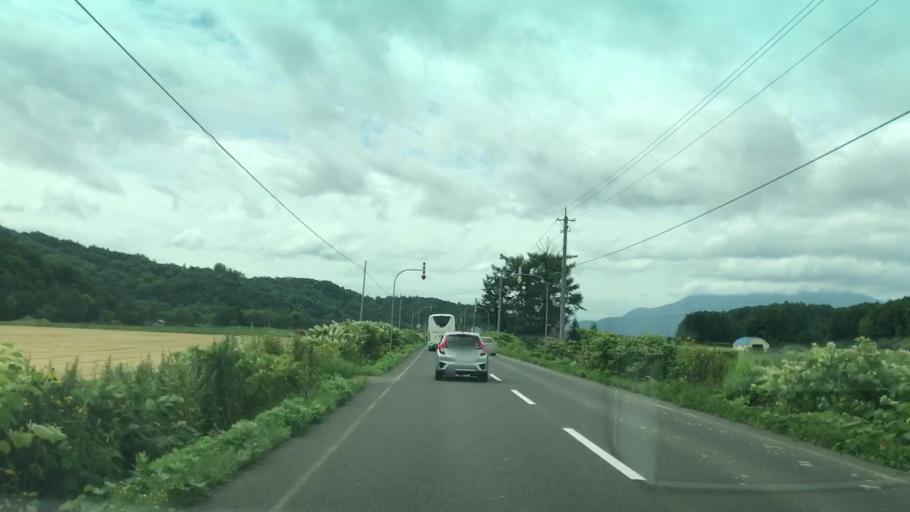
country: JP
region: Hokkaido
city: Niseko Town
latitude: 42.9436
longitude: 140.8201
